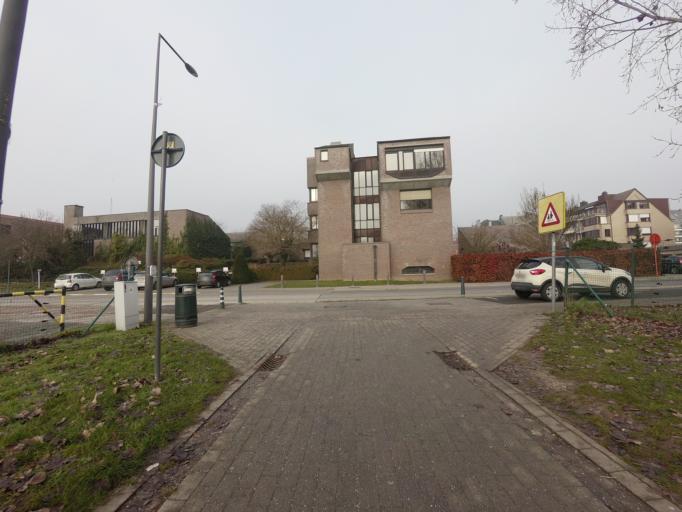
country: BE
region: Flanders
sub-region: Provincie Oost-Vlaanderen
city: Ninove
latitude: 50.8321
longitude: 4.0193
